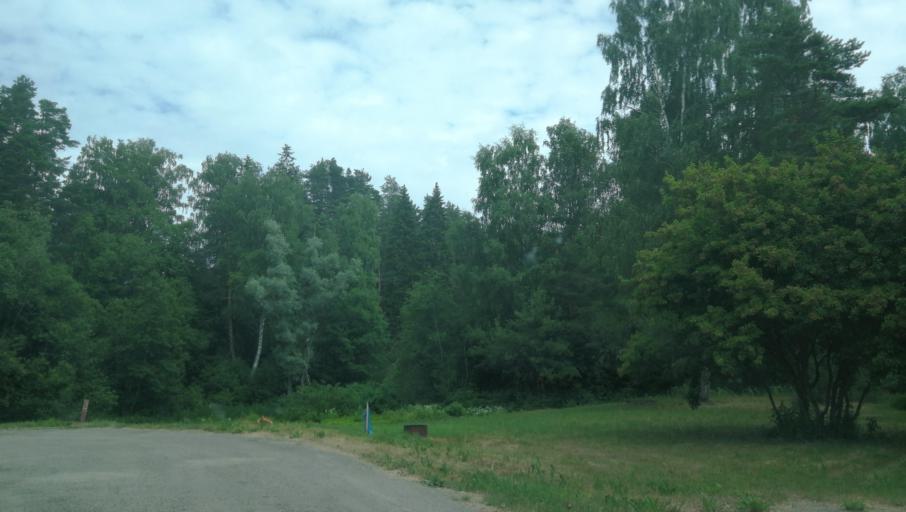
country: LV
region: Naukseni
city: Naukseni
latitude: 57.7866
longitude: 25.4246
